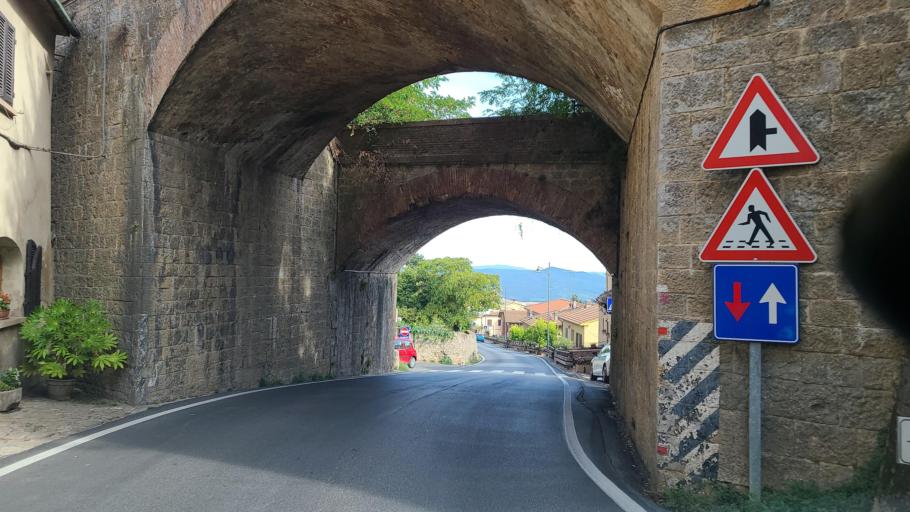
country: IT
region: Tuscany
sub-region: Province of Pisa
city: Volterra
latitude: 43.3994
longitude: 10.8719
